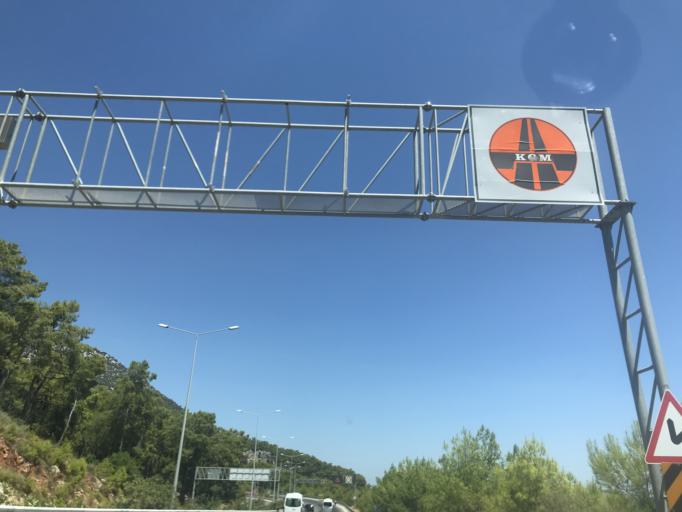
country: TR
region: Antalya
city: Cakirlar
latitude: 36.7562
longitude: 30.5689
